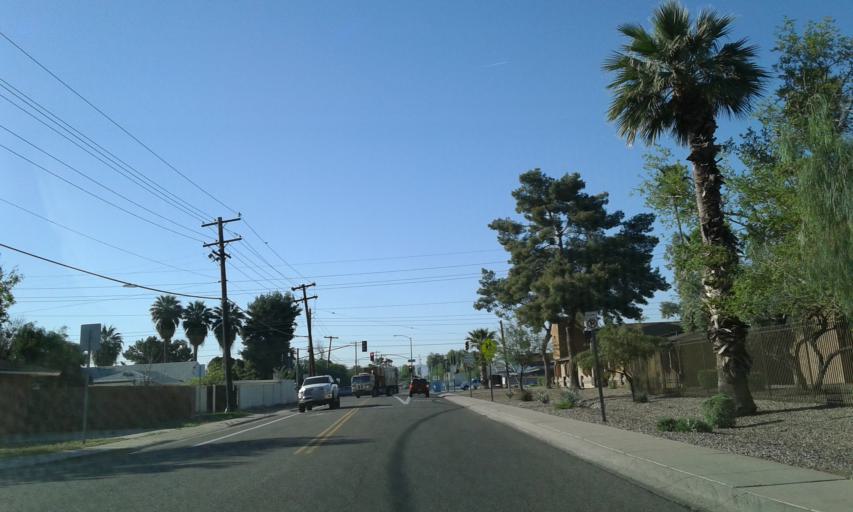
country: US
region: Arizona
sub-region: Maricopa County
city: Phoenix
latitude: 33.4818
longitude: -112.1085
